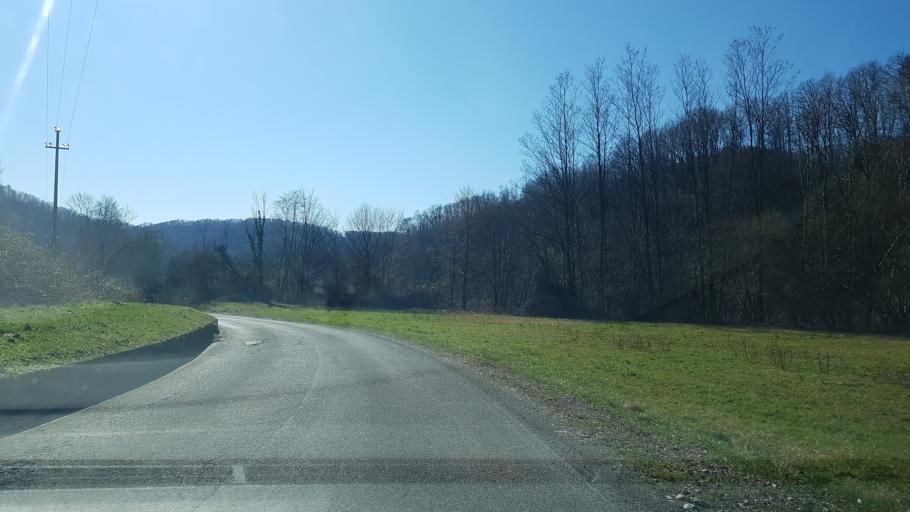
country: IT
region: Friuli Venezia Giulia
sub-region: Provincia di Udine
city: Nimis
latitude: 46.2129
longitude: 13.2922
